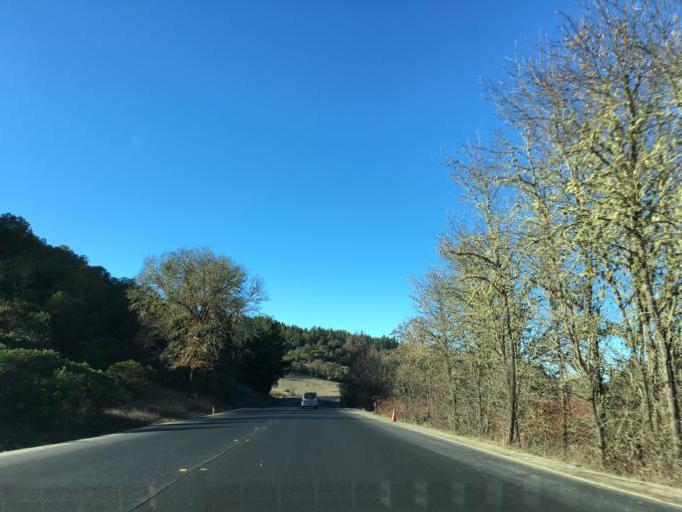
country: US
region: California
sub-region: Mendocino County
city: Laytonville
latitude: 39.6321
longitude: -123.4651
